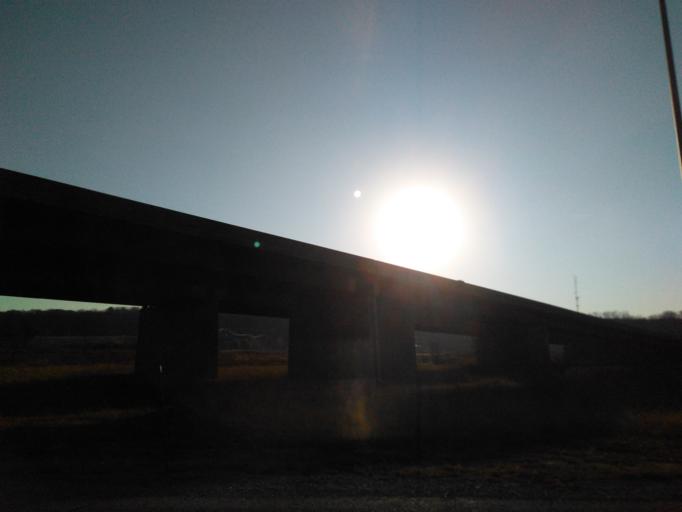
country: US
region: Illinois
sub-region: Saint Clair County
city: Dupo
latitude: 38.5297
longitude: -90.1965
